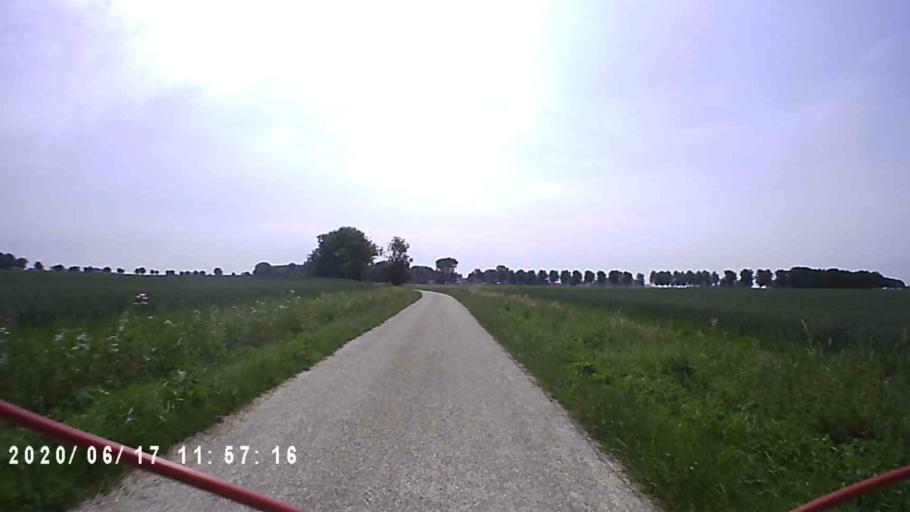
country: NL
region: Groningen
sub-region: Gemeente De Marne
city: Ulrum
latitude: 53.3468
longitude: 6.3235
